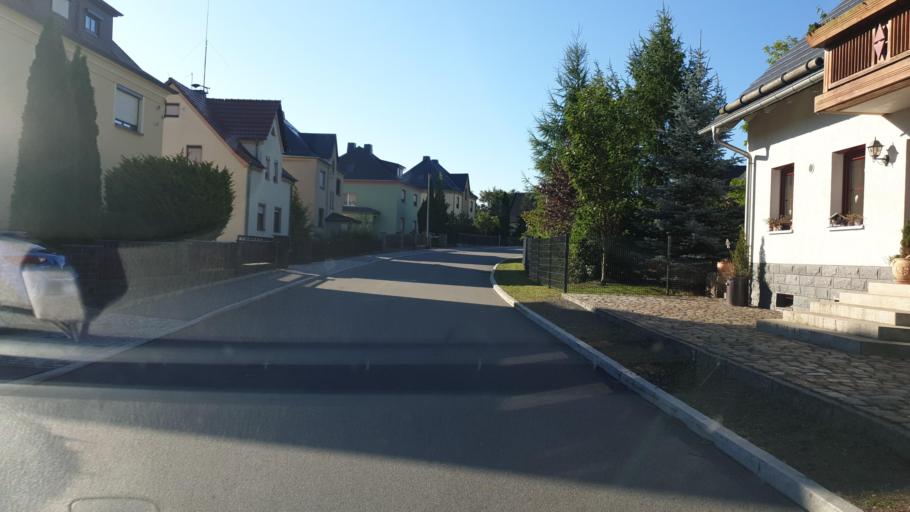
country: DE
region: Saxony
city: Lichtentanne
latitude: 50.6657
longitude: 12.4364
